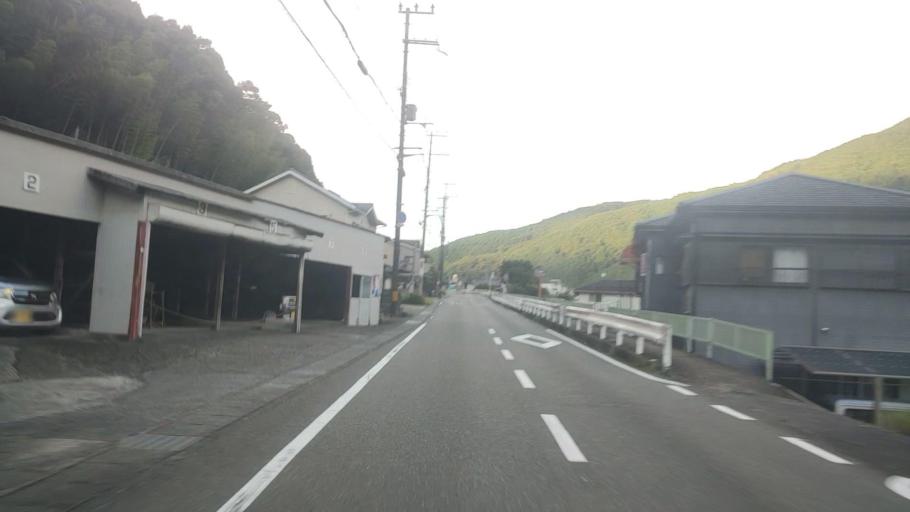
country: JP
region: Wakayama
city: Tanabe
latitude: 33.7896
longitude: 135.5151
